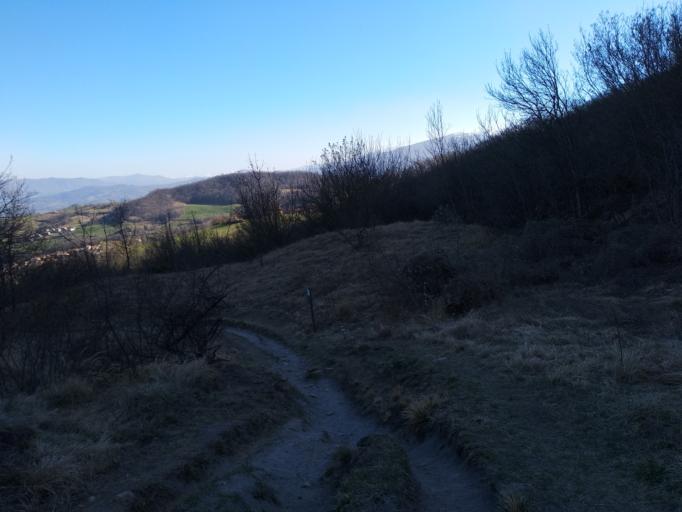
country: IT
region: Emilia-Romagna
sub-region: Provincia di Reggio Emilia
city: Castelnovo ne'Monti
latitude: 44.4249
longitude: 10.4191
